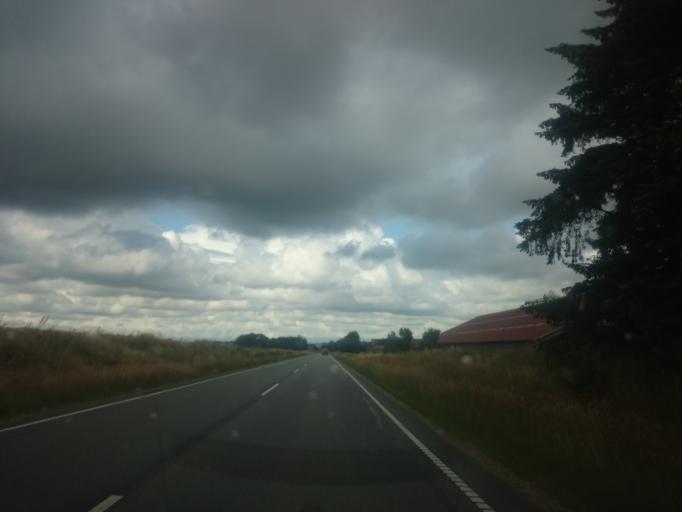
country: DK
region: South Denmark
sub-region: Billund Kommune
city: Grindsted
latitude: 55.6839
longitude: 8.9632
